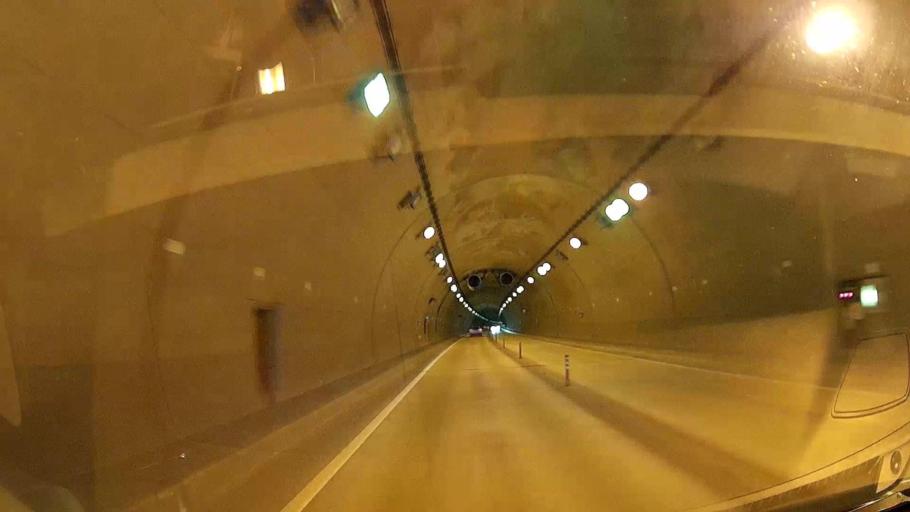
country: JP
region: Shizuoka
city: Shizuoka-shi
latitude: 35.0227
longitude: 138.3851
